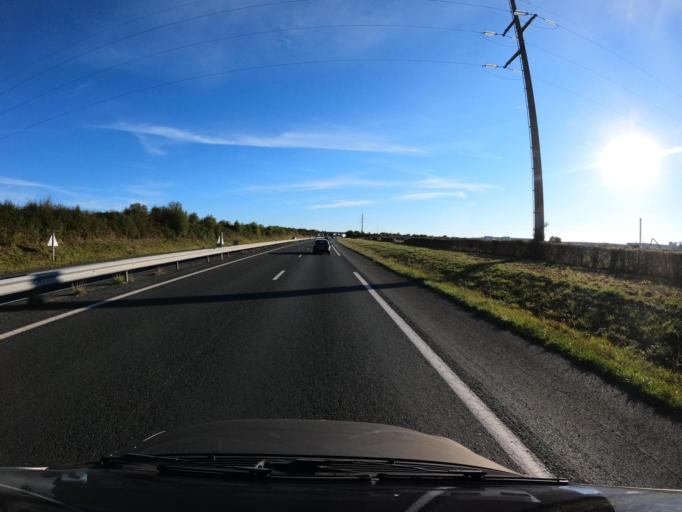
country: FR
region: Pays de la Loire
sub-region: Departement de Maine-et-Loire
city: Mazieres-en-Mauges
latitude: 47.0676
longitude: -0.8267
